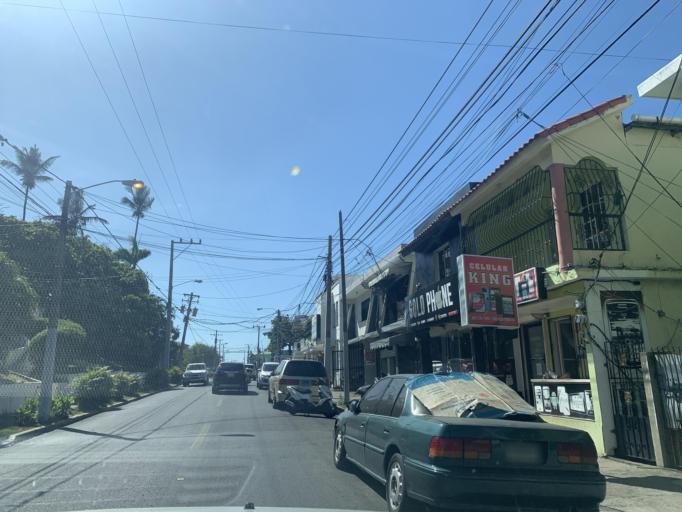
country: DO
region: Puerto Plata
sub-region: Puerto Plata
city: Puerto Plata
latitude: 19.7934
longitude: -70.6835
